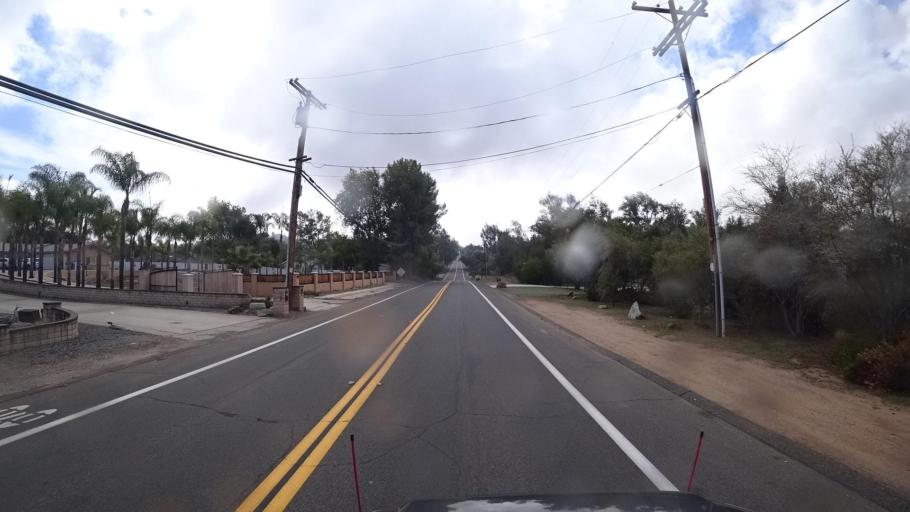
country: US
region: California
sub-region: San Diego County
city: Granite Hills
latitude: 32.7867
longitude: -116.9062
